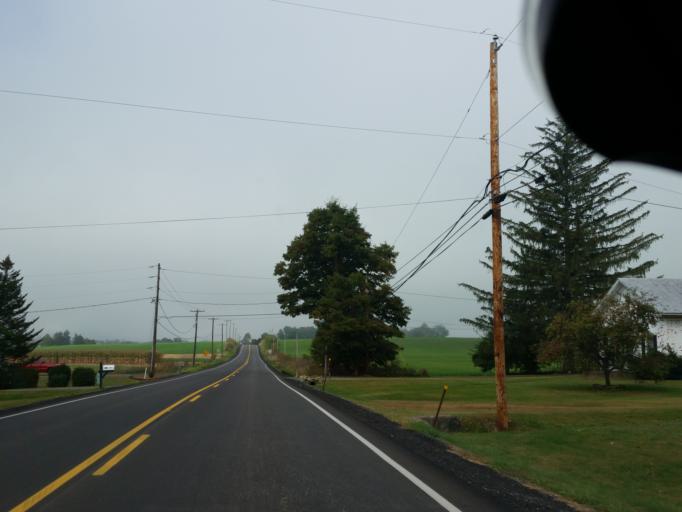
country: US
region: Pennsylvania
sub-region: Northumberland County
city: Dewart
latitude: 41.1147
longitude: -76.9304
